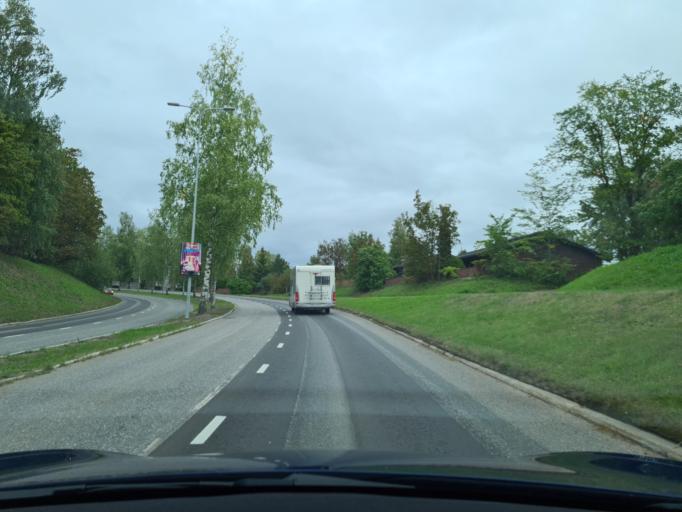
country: FI
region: South Karelia
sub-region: Lappeenranta
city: Lappeenranta
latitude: 61.0497
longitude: 28.1845
